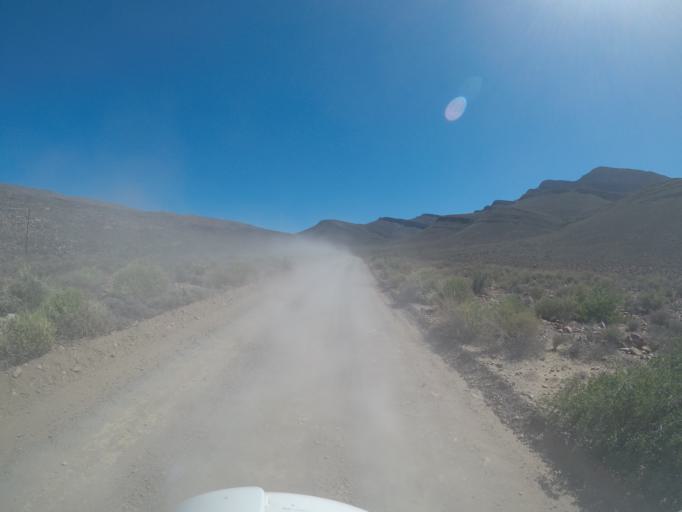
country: ZA
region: Western Cape
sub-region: West Coast District Municipality
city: Clanwilliam
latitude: -32.6328
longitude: 19.3969
